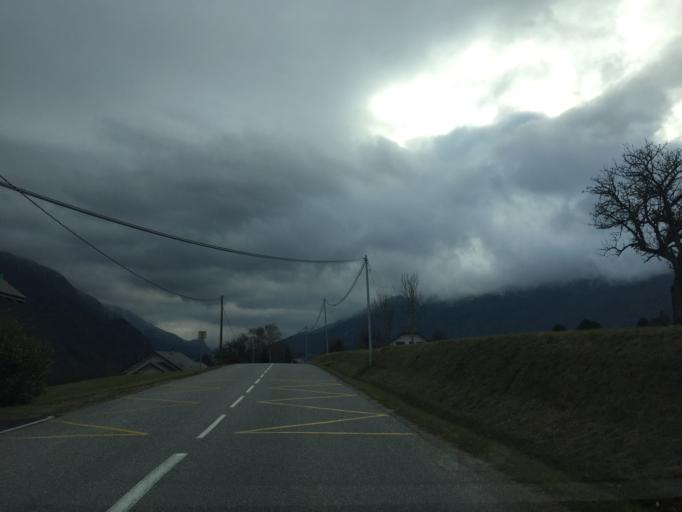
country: FR
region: Rhone-Alpes
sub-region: Departement de la Savoie
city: Vimines
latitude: 45.5439
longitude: 5.8669
